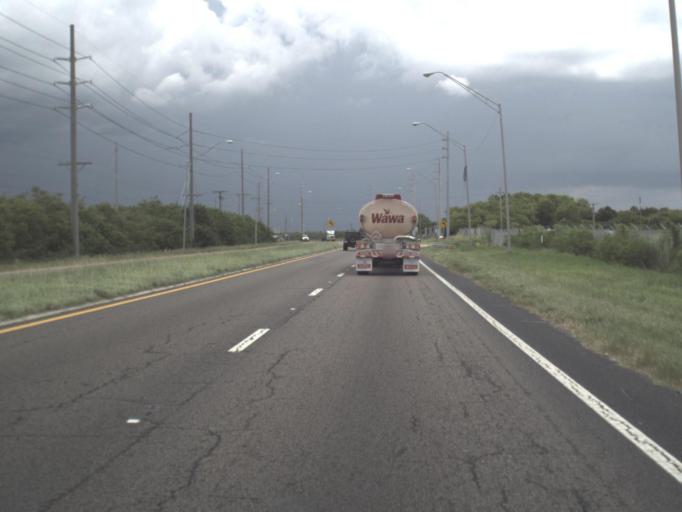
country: US
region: Florida
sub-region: Hillsborough County
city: Palm River-Clair Mel
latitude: 27.9259
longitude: -82.4218
